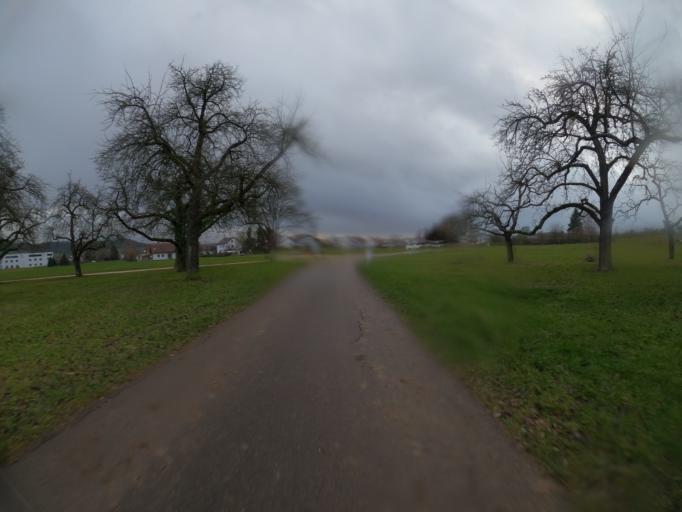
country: DE
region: Baden-Wuerttemberg
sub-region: Regierungsbezirk Stuttgart
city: Waschenbeuren
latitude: 48.7645
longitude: 9.6948
